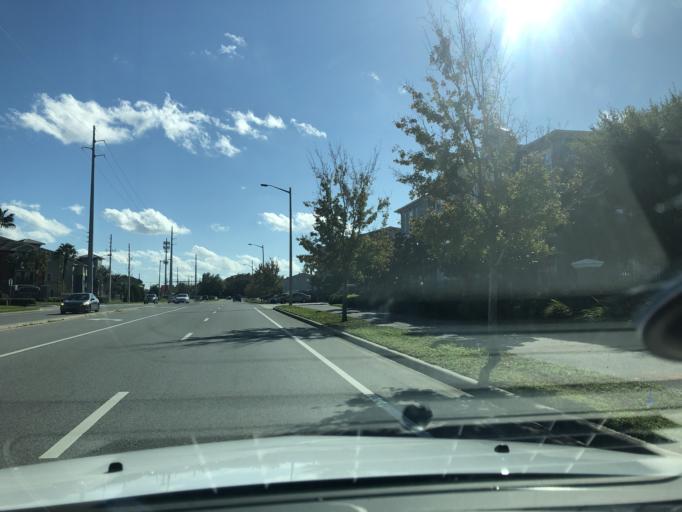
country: US
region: Florida
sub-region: Orange County
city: Oak Ridge
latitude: 28.4750
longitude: -81.4424
